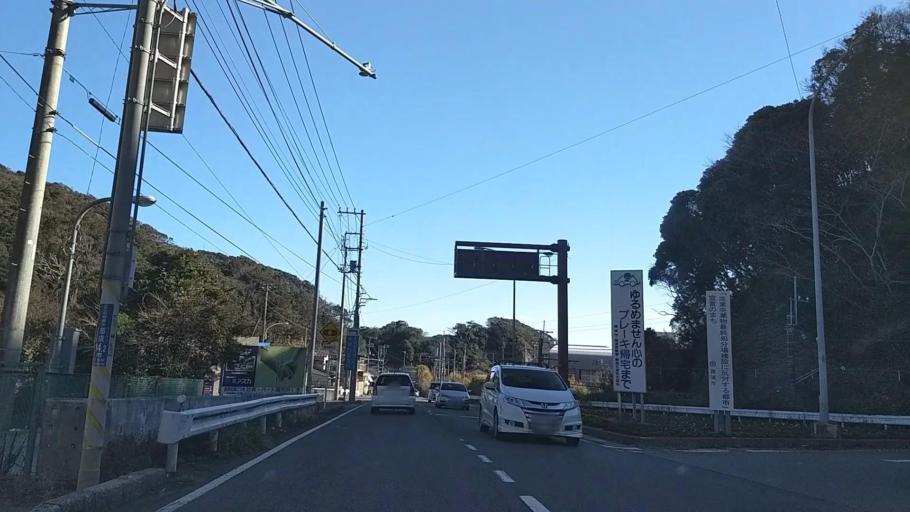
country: JP
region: Chiba
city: Katsuura
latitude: 35.1411
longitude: 140.2698
